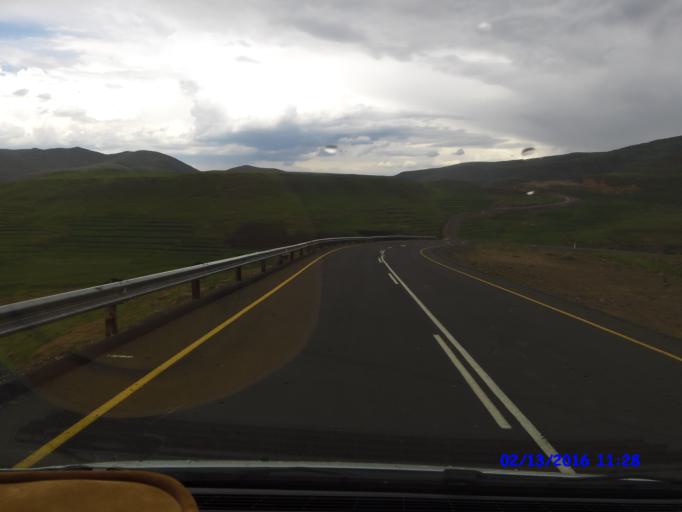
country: LS
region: Maseru
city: Nako
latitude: -29.7751
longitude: 28.0235
